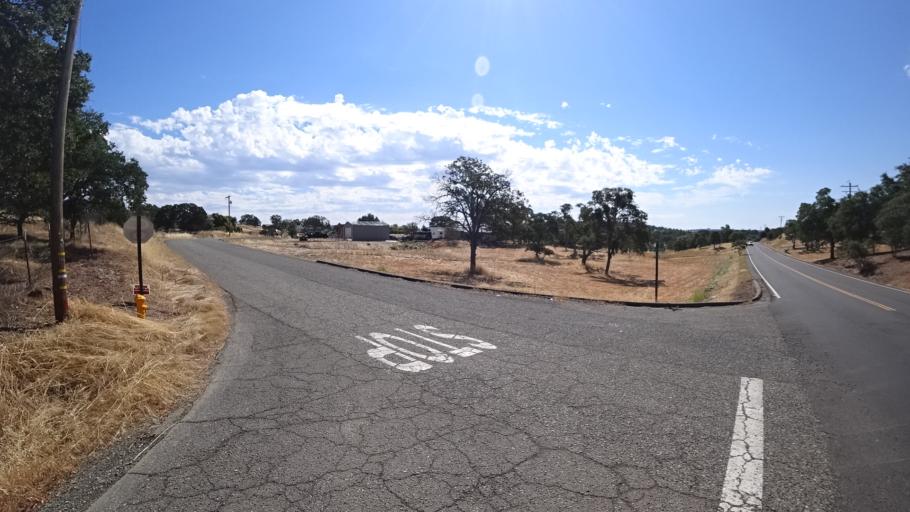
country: US
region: California
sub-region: Calaveras County
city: Copperopolis
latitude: 37.9170
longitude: -120.6262
